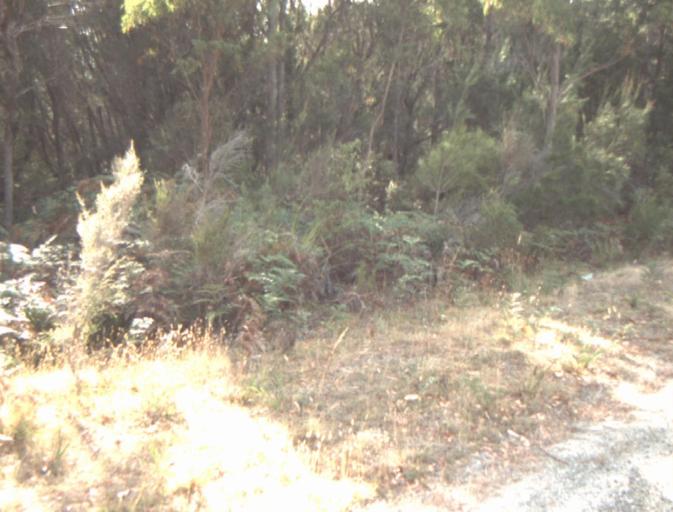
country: AU
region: Tasmania
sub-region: Dorset
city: Bridport
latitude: -41.1264
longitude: 147.2109
